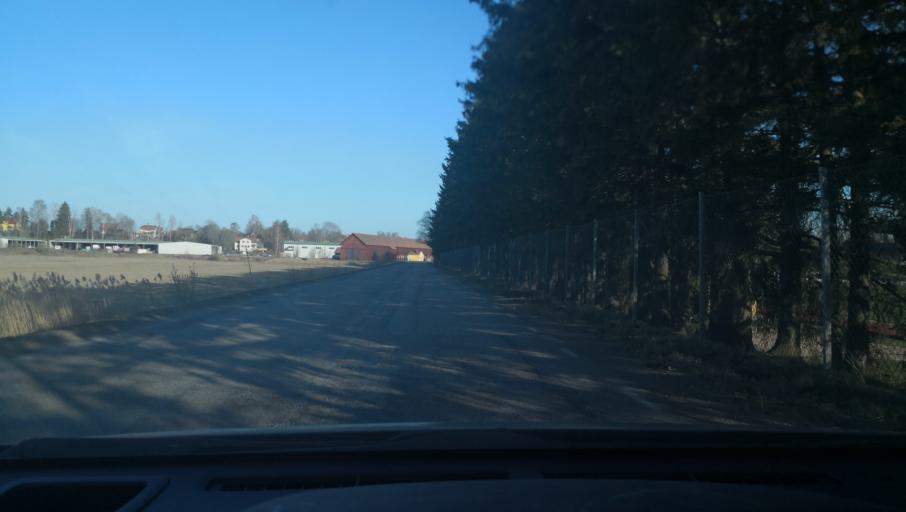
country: SE
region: Uppsala
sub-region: Heby Kommun
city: Heby
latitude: 59.9456
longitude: 16.8497
